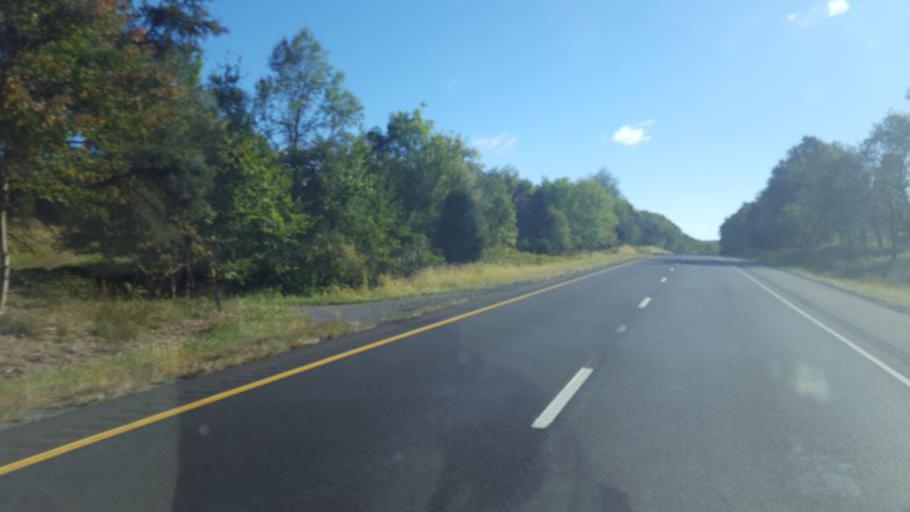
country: US
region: Maryland
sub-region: Washington County
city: Wilson-Conococheague
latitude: 39.6260
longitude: -77.9893
